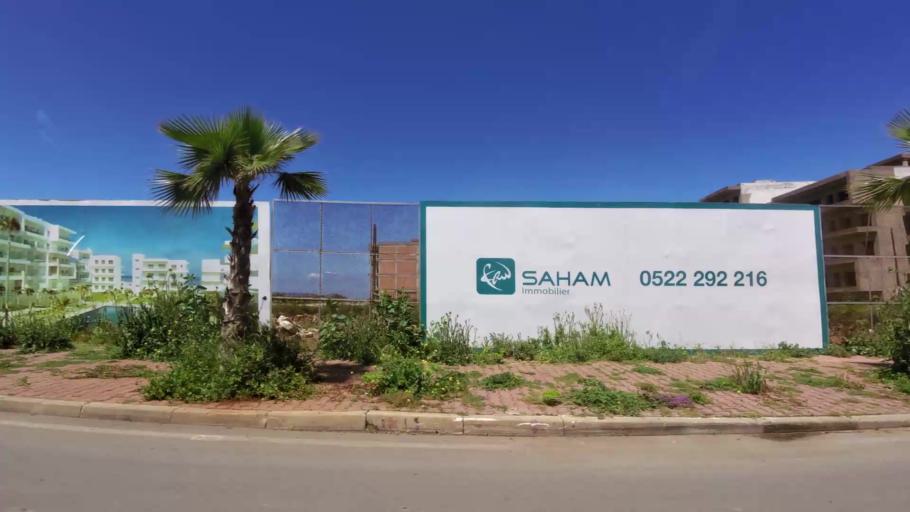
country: MA
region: Grand Casablanca
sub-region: Nouaceur
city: Dar Bouazza
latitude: 33.5330
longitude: -7.8229
